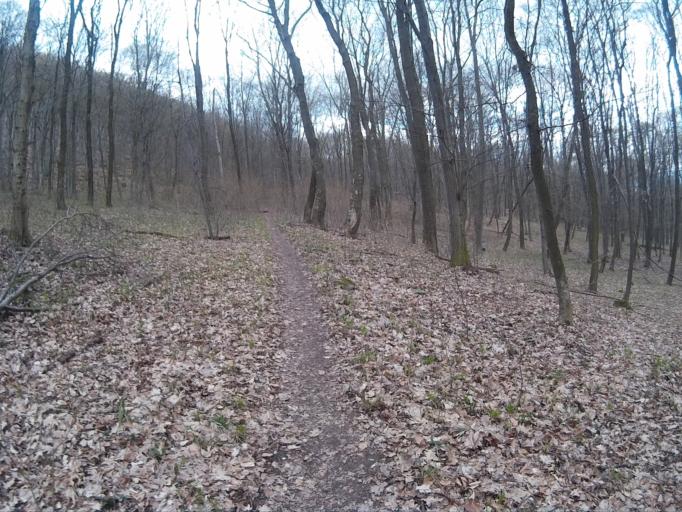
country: HU
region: Pest
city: Kosd
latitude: 47.8405
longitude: 19.1415
